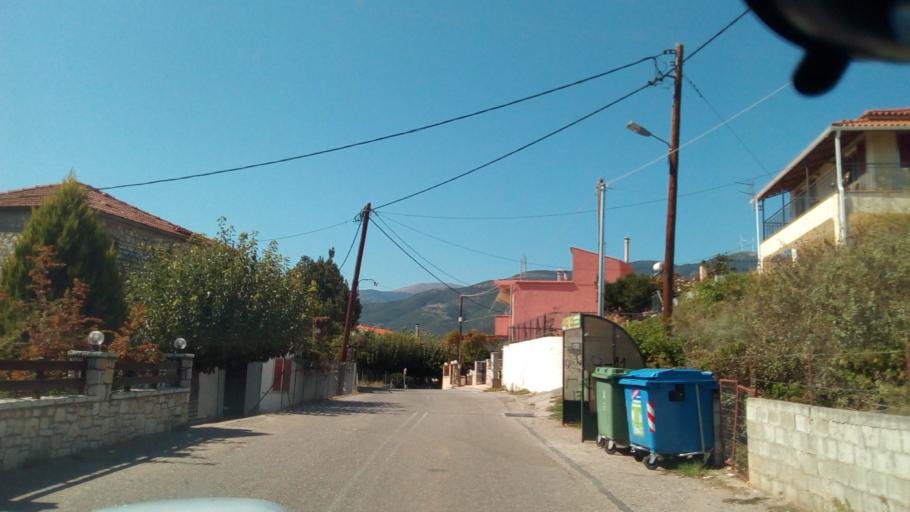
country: GR
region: West Greece
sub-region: Nomos Aitolias kai Akarnanias
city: Nafpaktos
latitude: 38.4166
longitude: 21.8977
